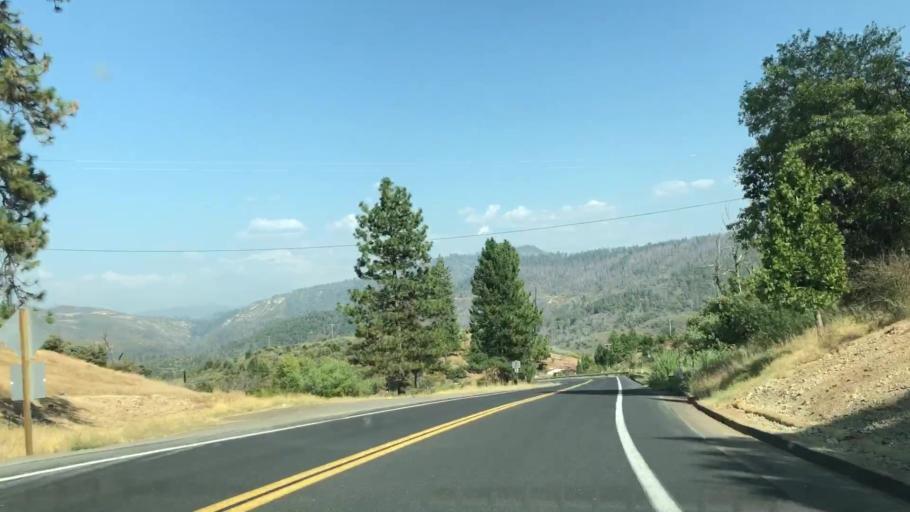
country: US
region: California
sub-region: Tuolumne County
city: Tuolumne City
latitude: 37.8227
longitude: -120.0254
